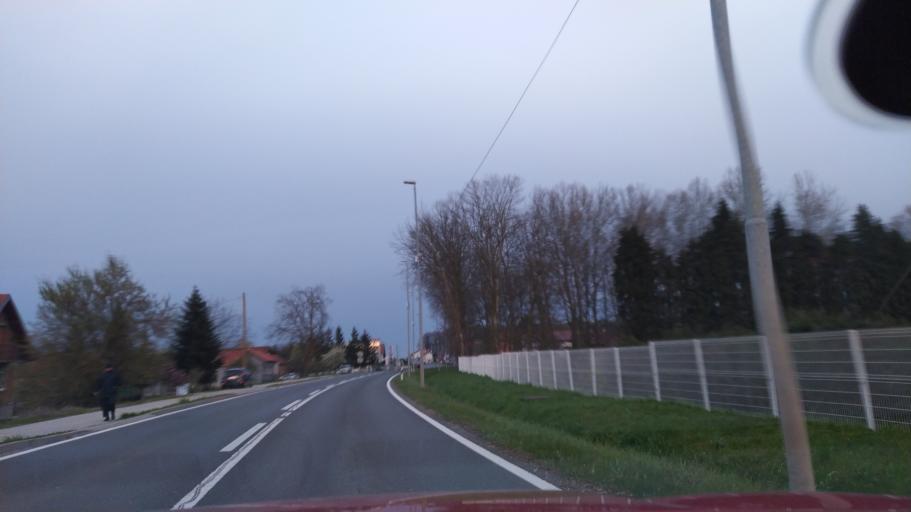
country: HR
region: Koprivnicko-Krizevacka
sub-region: Grad Koprivnica
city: Koprivnica
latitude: 46.1805
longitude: 16.7876
